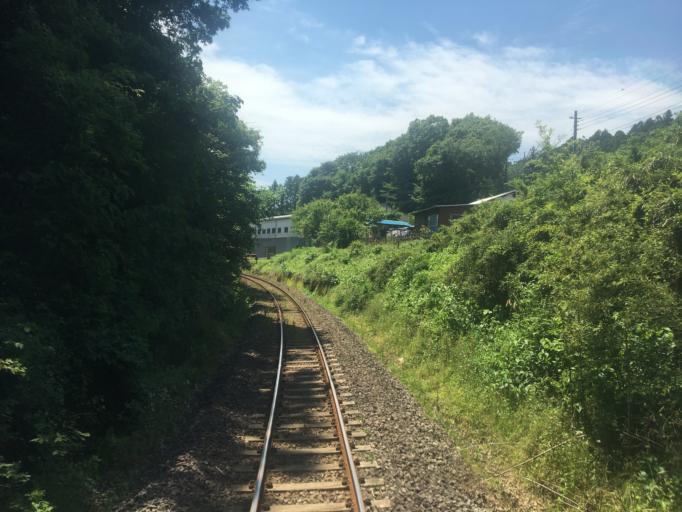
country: JP
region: Saitama
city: Ogawa
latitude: 36.0331
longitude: 139.2626
